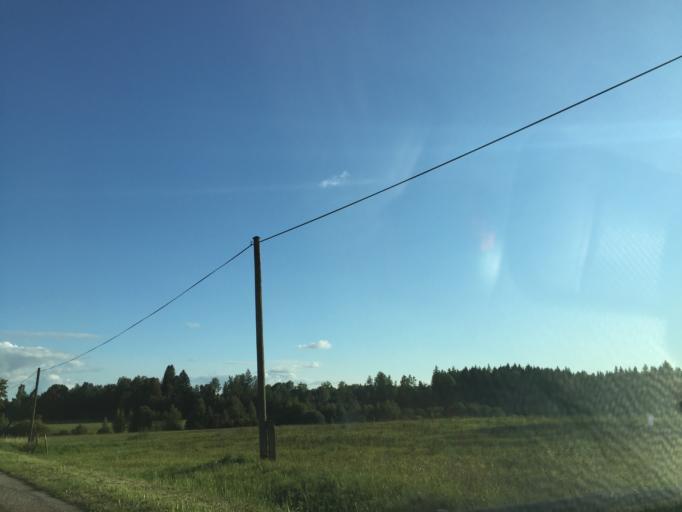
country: LV
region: Krimulda
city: Ragana
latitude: 57.1933
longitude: 24.7069
